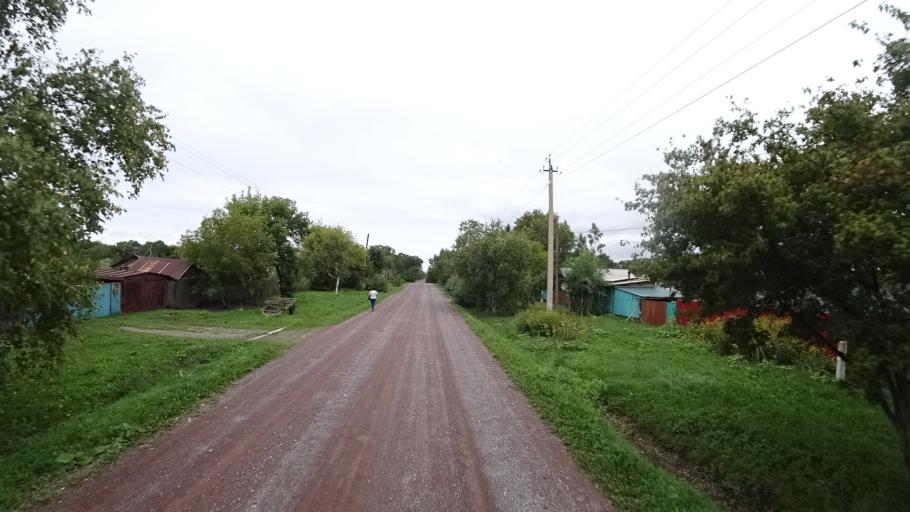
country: RU
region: Primorskiy
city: Chernigovka
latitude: 44.3381
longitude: 132.5918
